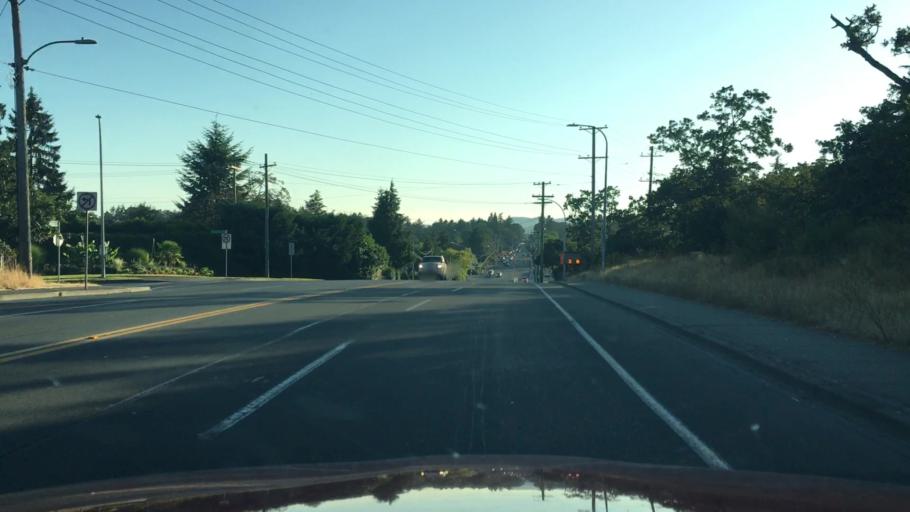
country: CA
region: British Columbia
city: Victoria
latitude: 48.4711
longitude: -123.3568
